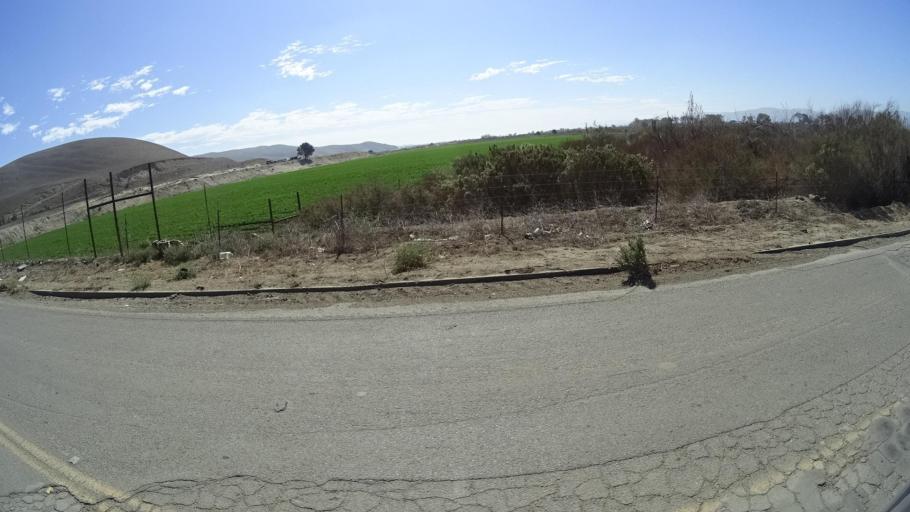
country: US
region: California
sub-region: Monterey County
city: Greenfield
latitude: 36.3397
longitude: -121.2026
